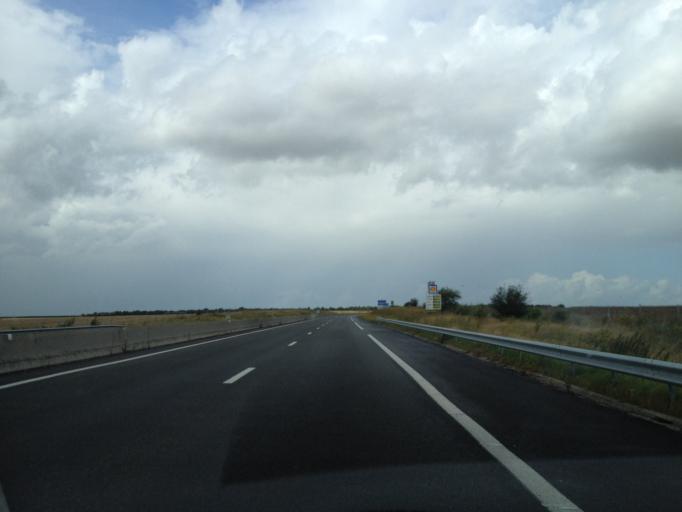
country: FR
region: Picardie
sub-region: Departement de la Somme
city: Sailly-Flibeaucourt
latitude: 50.1630
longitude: 1.7692
